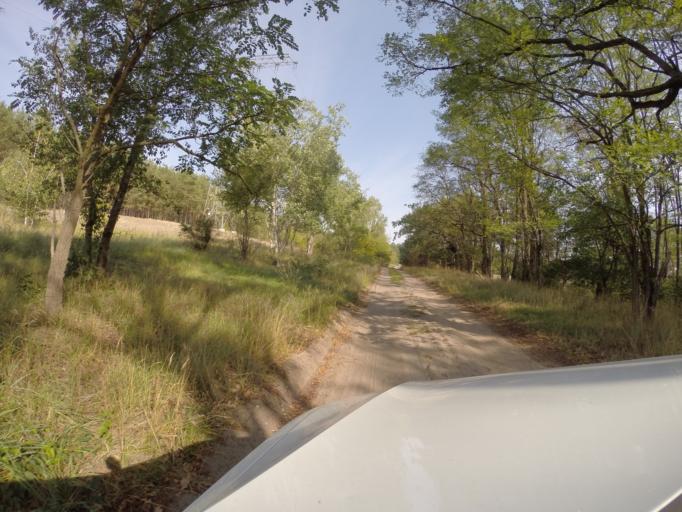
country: DE
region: Brandenburg
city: Baruth
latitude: 52.1251
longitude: 13.5143
